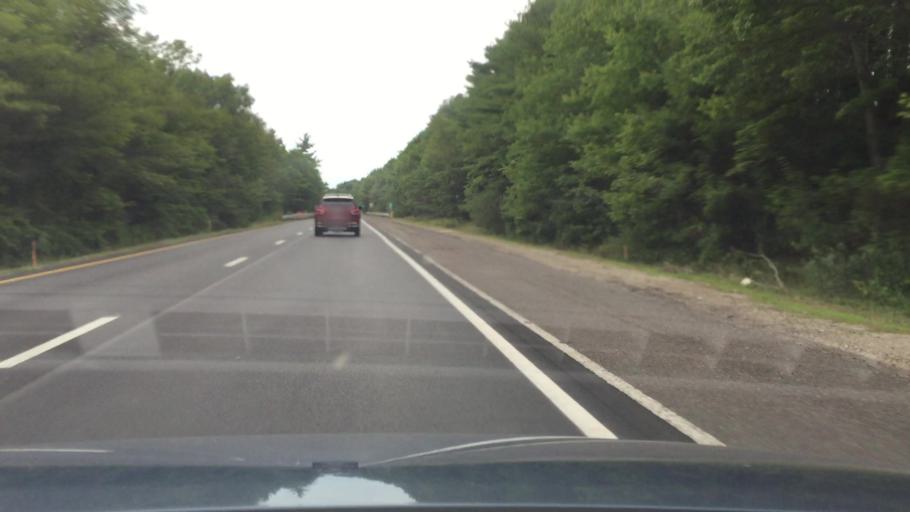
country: US
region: Massachusetts
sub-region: Plymouth County
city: Marshfield
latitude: 42.0609
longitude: -70.7265
